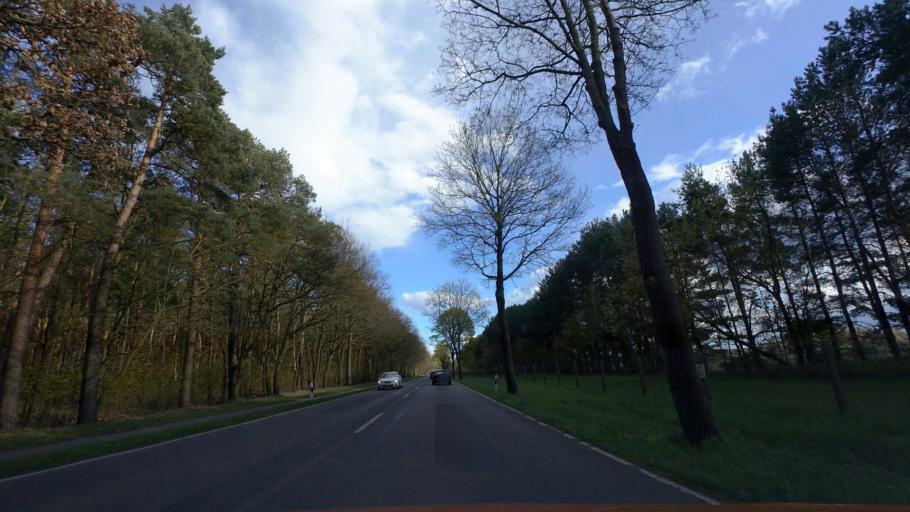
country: DE
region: Brandenburg
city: Kyritz
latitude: 52.9201
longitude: 12.4291
